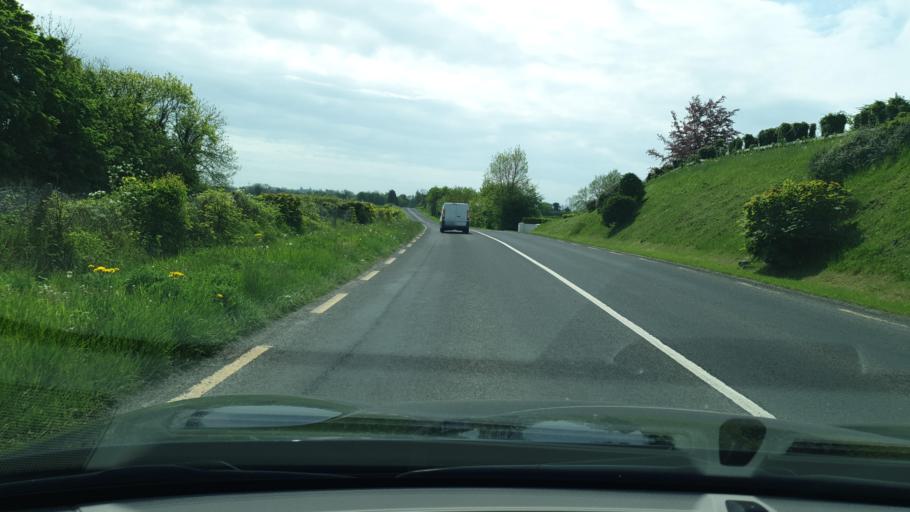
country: IE
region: Leinster
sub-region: An Mhi
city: Navan
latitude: 53.7582
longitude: -6.7243
